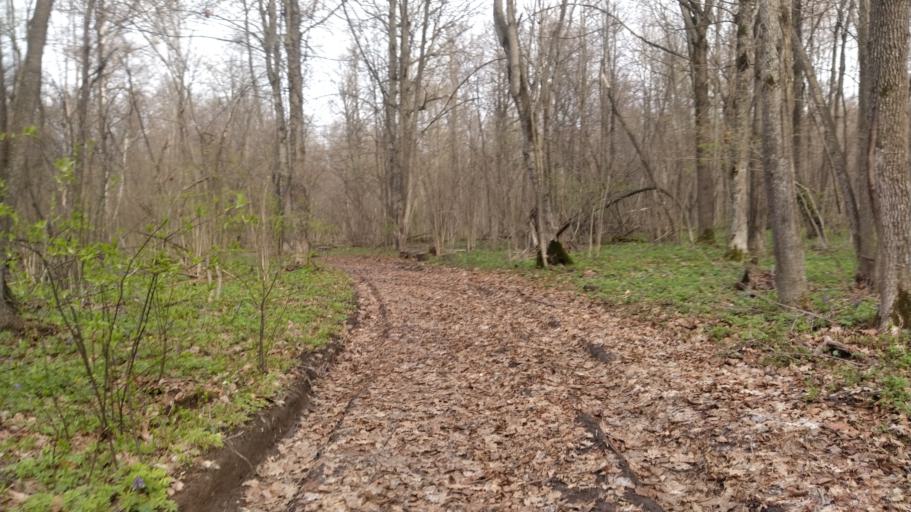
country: RU
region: Chuvashia
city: Novyye Lapsary
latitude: 56.1365
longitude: 47.1186
